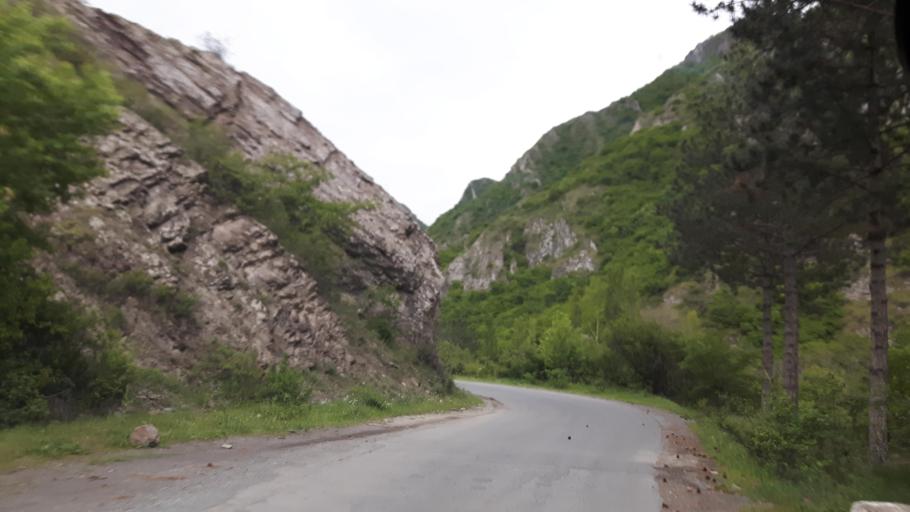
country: GE
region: Shida Kartli
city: Gori
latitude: 41.9003
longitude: 44.0751
